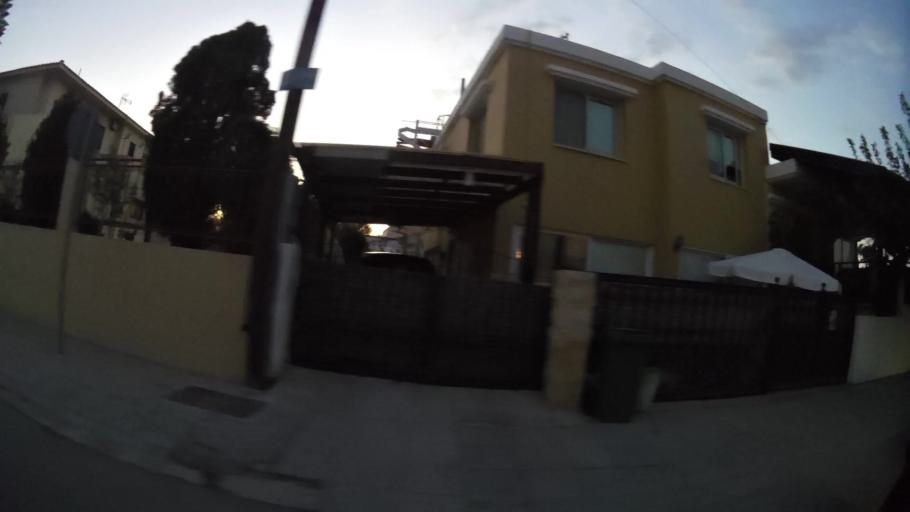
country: CY
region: Larnaka
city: Larnaca
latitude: 34.9128
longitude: 33.5900
